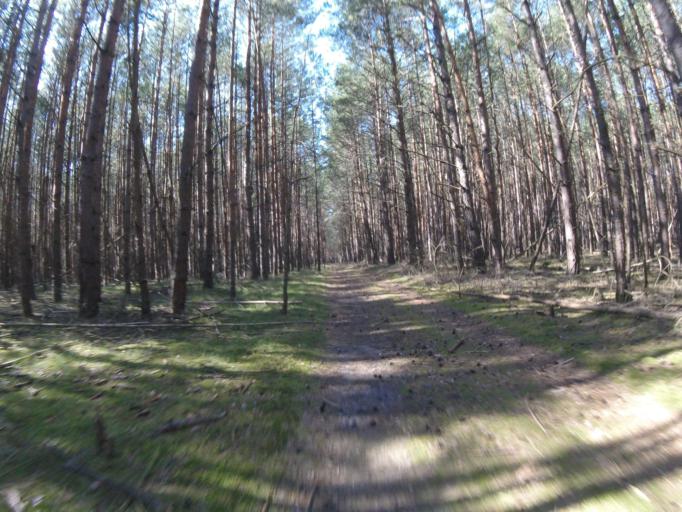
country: DE
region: Brandenburg
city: Bestensee
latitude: 52.2621
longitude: 13.6834
